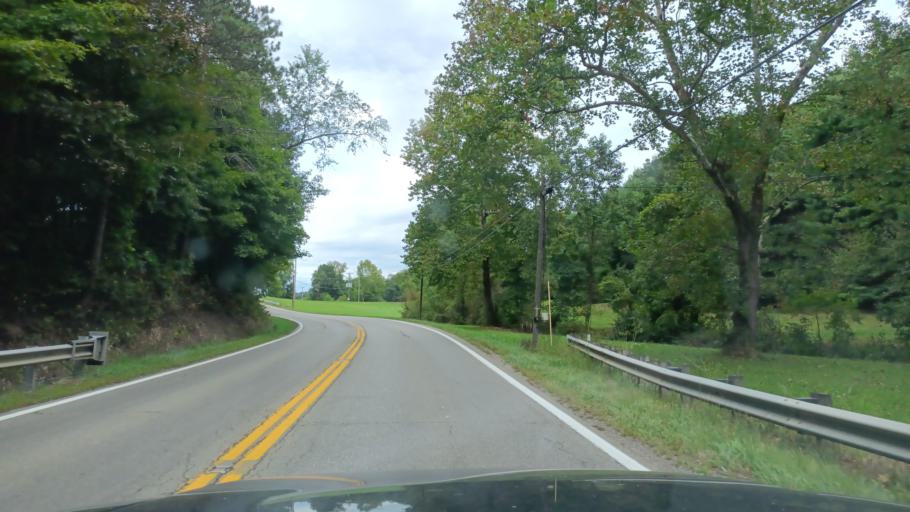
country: US
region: Ohio
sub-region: Vinton County
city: McArthur
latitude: 39.2676
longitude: -82.5144
